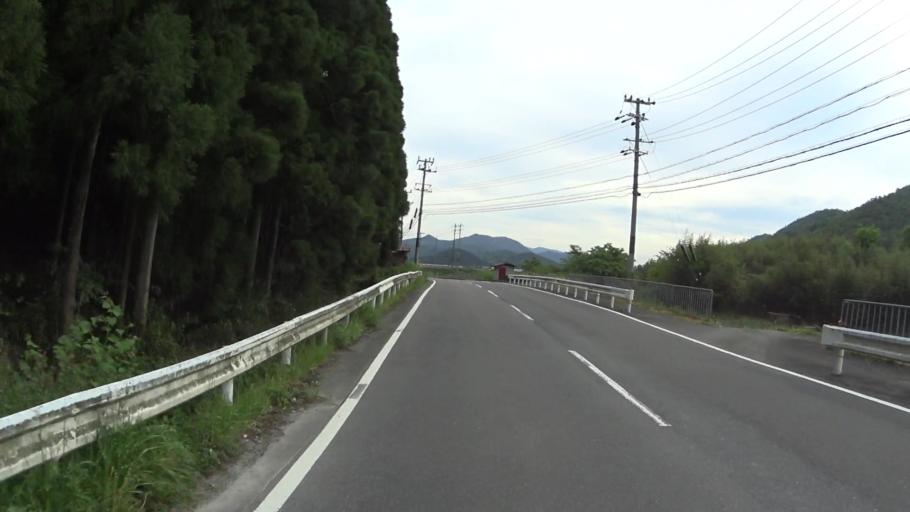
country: JP
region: Kyoto
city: Kameoka
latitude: 35.1048
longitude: 135.5177
